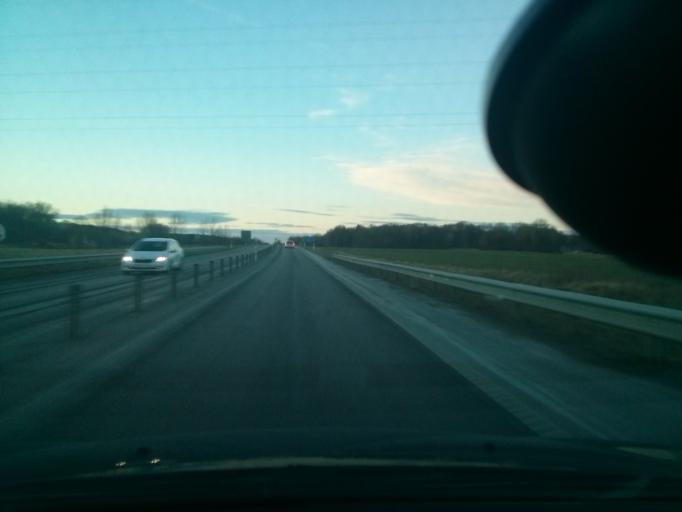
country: SE
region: Blekinge
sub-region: Ronneby Kommun
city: Kallinge
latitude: 56.2346
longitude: 15.2585
